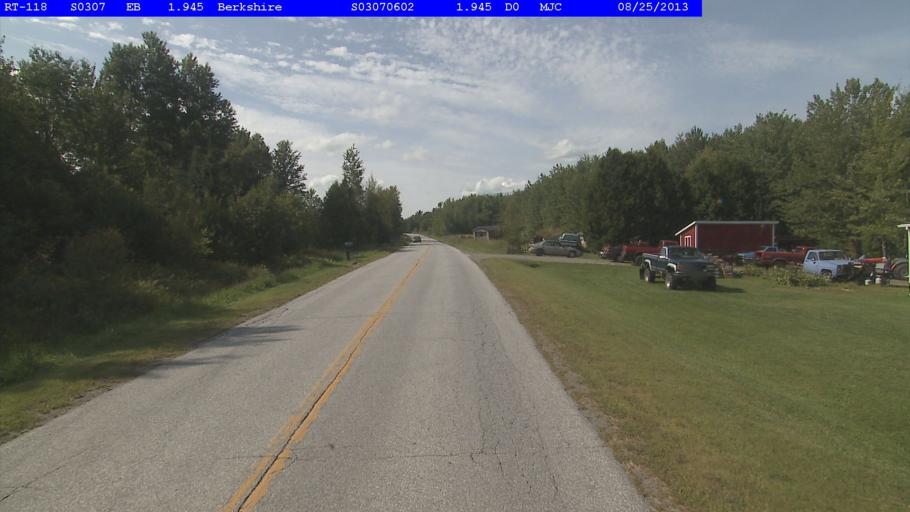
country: US
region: Vermont
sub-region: Franklin County
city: Enosburg Falls
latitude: 44.9472
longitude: -72.7432
